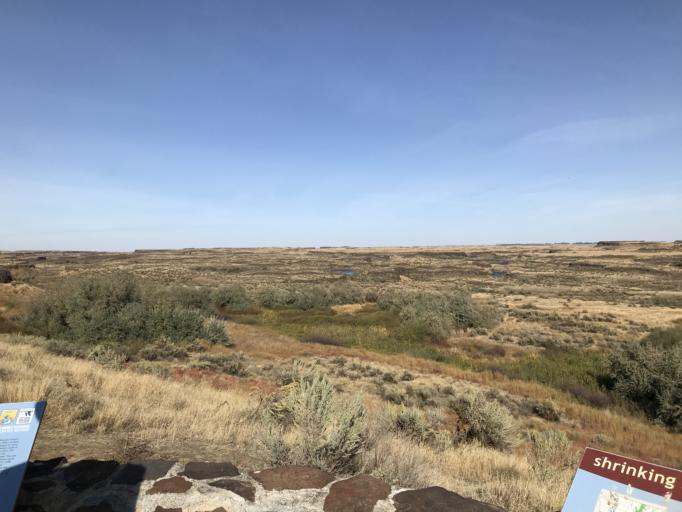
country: US
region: Washington
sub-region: Adams County
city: Othello
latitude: 46.9038
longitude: -119.3060
